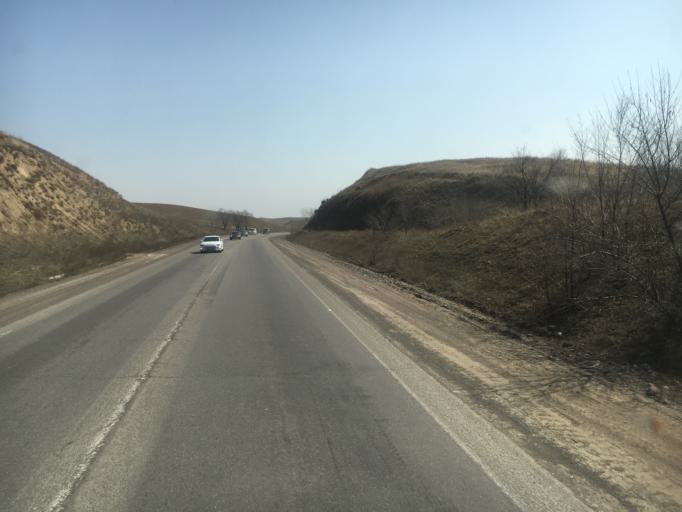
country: KZ
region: Almaty Oblysy
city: Burunday
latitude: 43.3044
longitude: 76.2193
